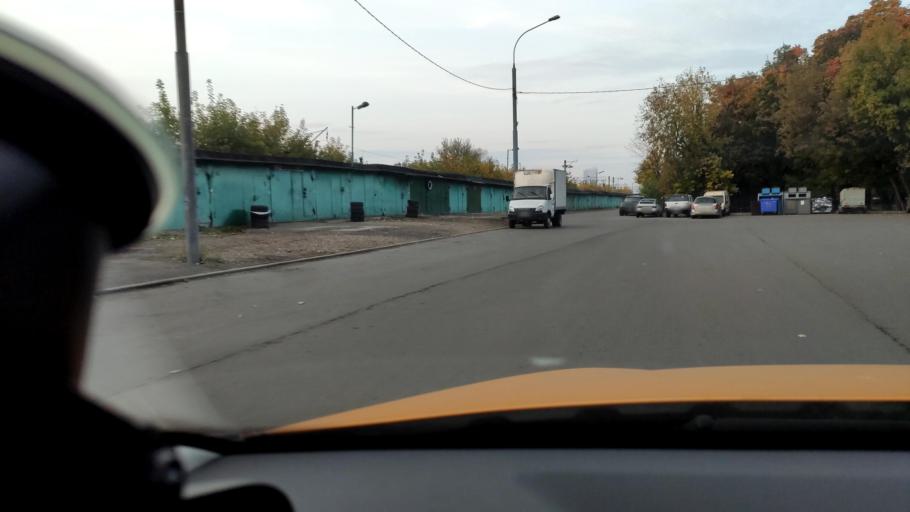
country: RU
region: Moscow
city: Vatutino
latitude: 55.8619
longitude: 37.6810
